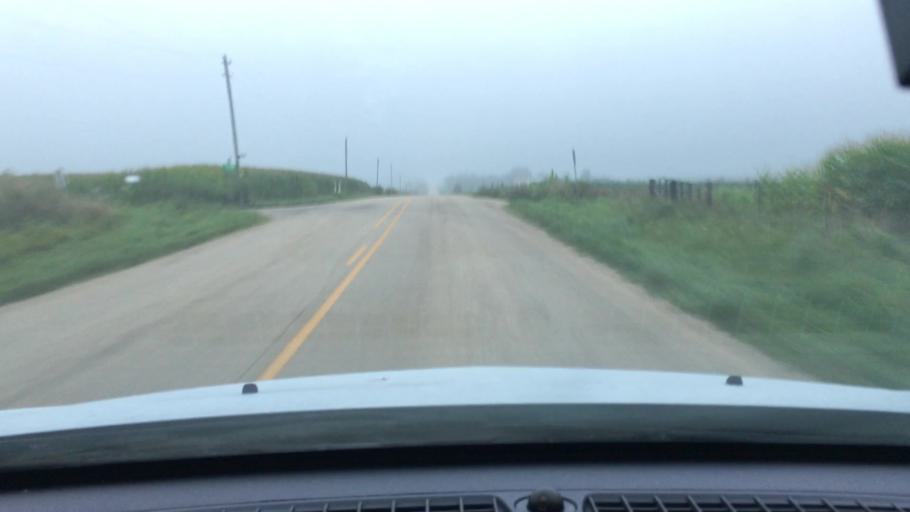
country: US
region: Illinois
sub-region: DeKalb County
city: Malta
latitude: 41.8626
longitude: -88.9614
